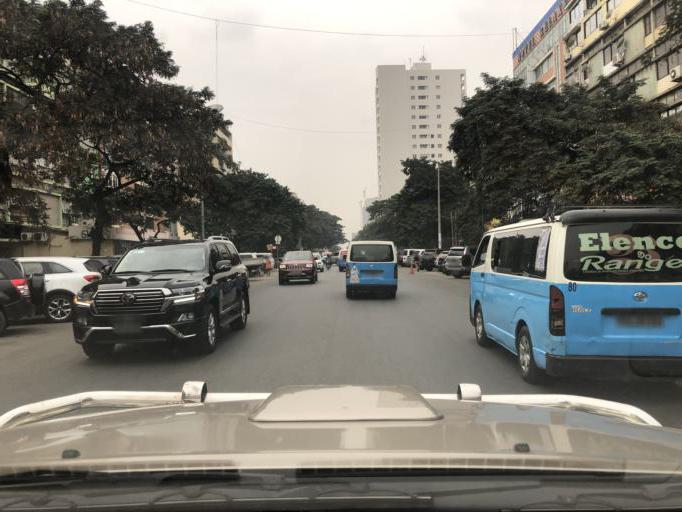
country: AO
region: Luanda
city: Luanda
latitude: -8.8205
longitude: 13.2475
